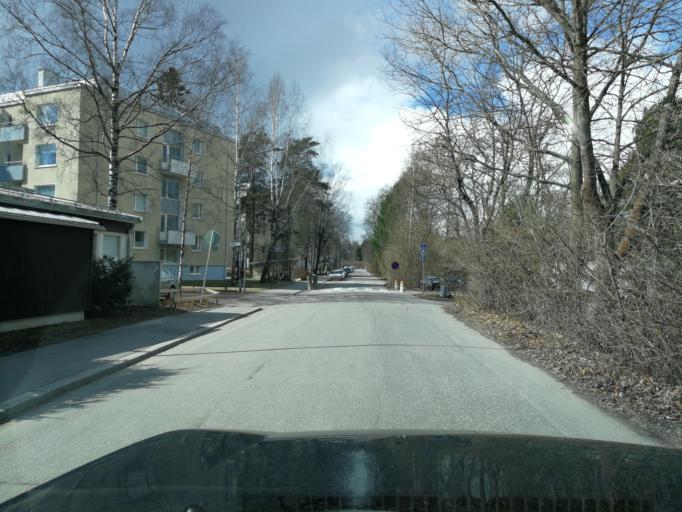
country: FI
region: Uusimaa
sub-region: Helsinki
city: Otaniemi
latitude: 60.1824
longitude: 24.8054
